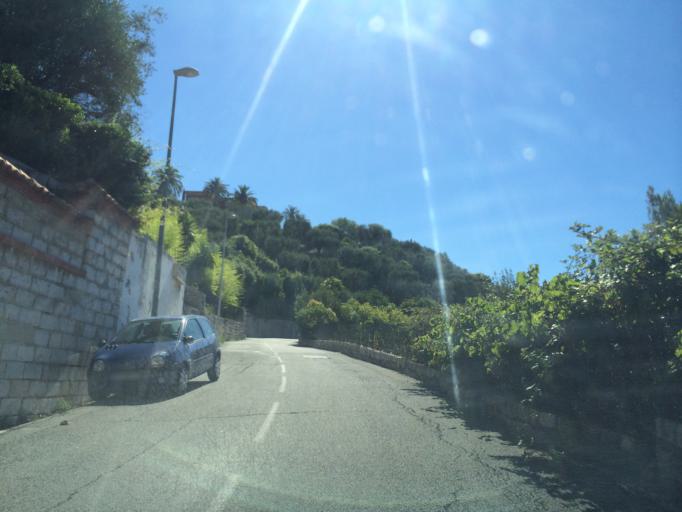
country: FR
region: Provence-Alpes-Cote d'Azur
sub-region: Departement des Alpes-Maritimes
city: Villefranche-sur-Mer
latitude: 43.7088
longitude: 7.3150
